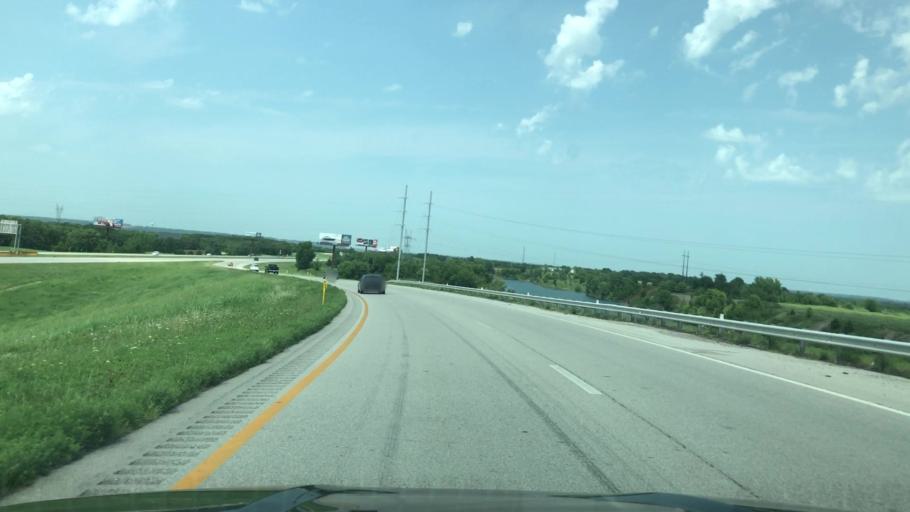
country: US
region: Oklahoma
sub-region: Rogers County
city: Catoosa
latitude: 36.1656
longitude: -95.7308
